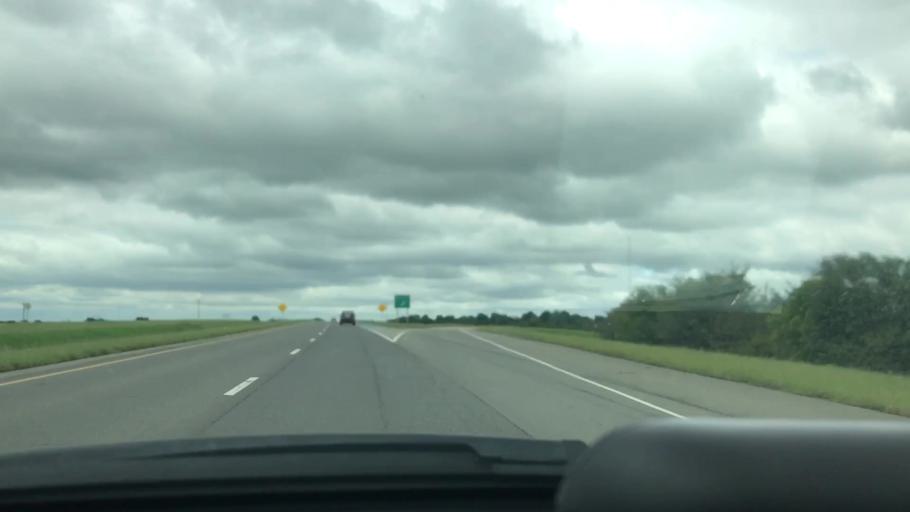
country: US
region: Oklahoma
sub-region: McIntosh County
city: Checotah
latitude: 35.5729
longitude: -95.4909
